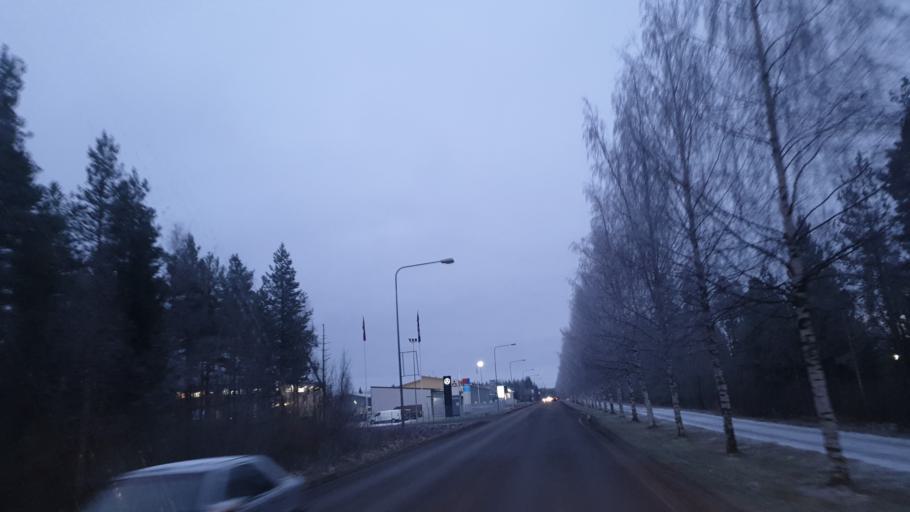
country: FI
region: Southern Ostrobothnia
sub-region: Seinaejoki
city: Nurmo
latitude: 62.7851
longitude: 22.9015
